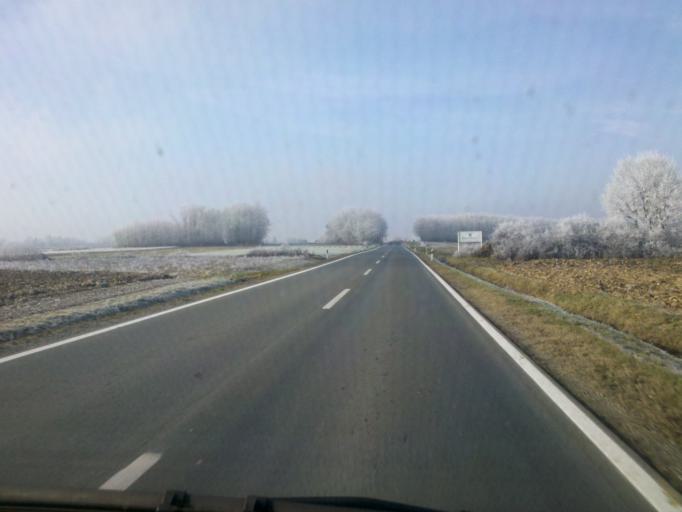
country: HR
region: Virovitick-Podravska
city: Pitomaca
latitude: 45.9706
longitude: 17.1812
